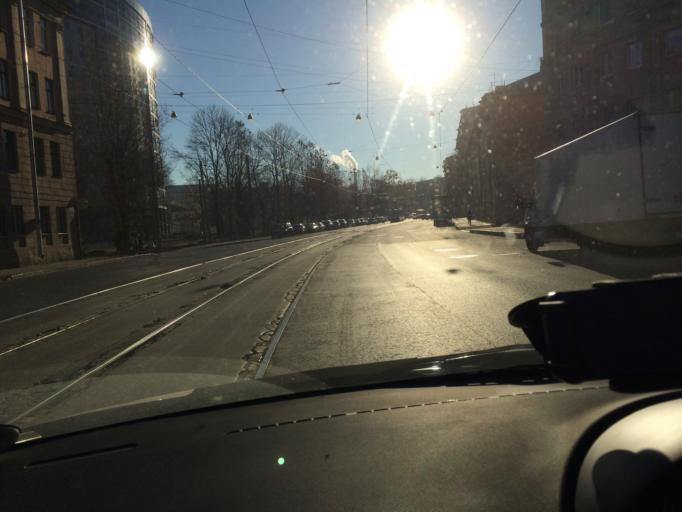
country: RU
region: St.-Petersburg
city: Obukhovo
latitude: 59.8680
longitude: 30.4644
